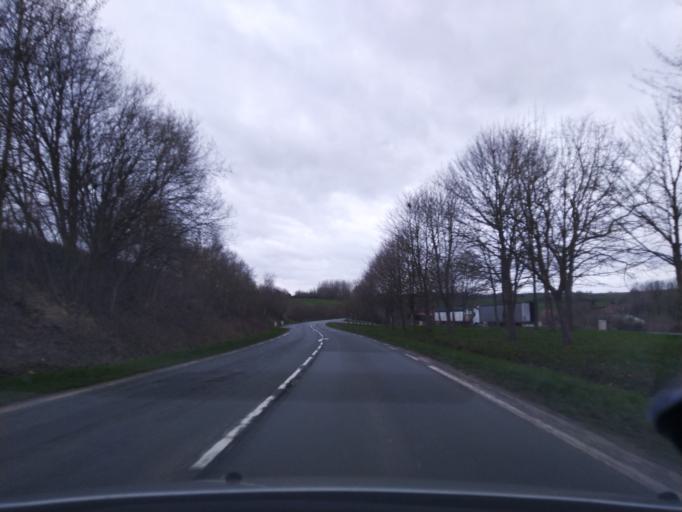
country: FR
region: Nord-Pas-de-Calais
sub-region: Departement du Pas-de-Calais
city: Divion
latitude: 50.4628
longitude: 2.4903
